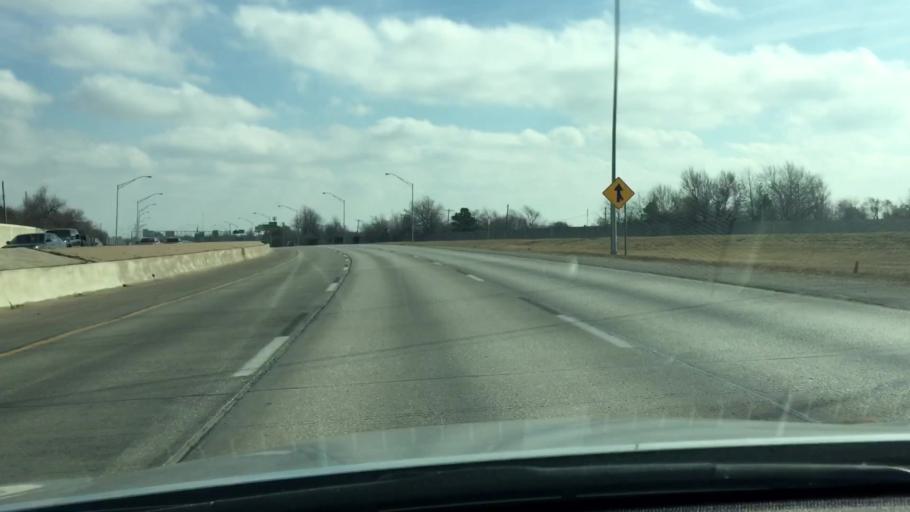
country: US
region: Oklahoma
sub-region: Oklahoma County
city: Oklahoma City
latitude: 35.3958
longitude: -97.5738
